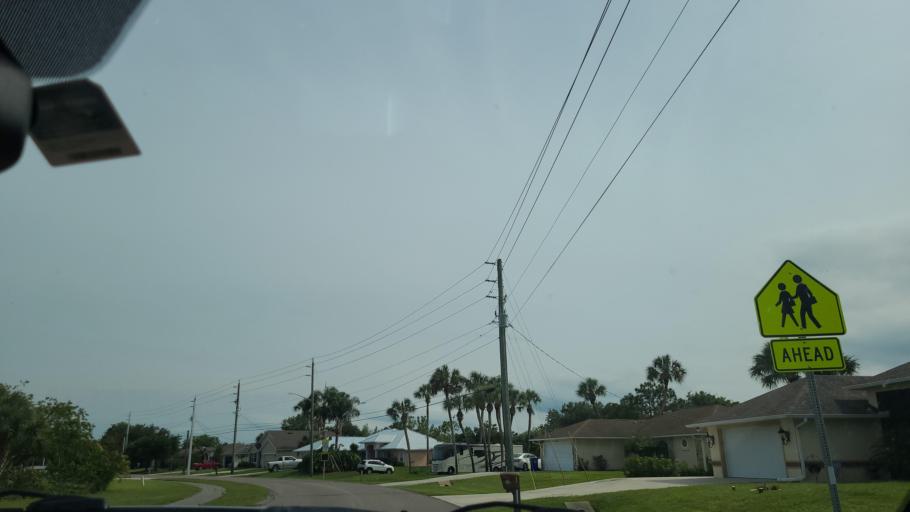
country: US
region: Florida
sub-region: Indian River County
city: Sebastian
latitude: 27.7653
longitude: -80.4660
